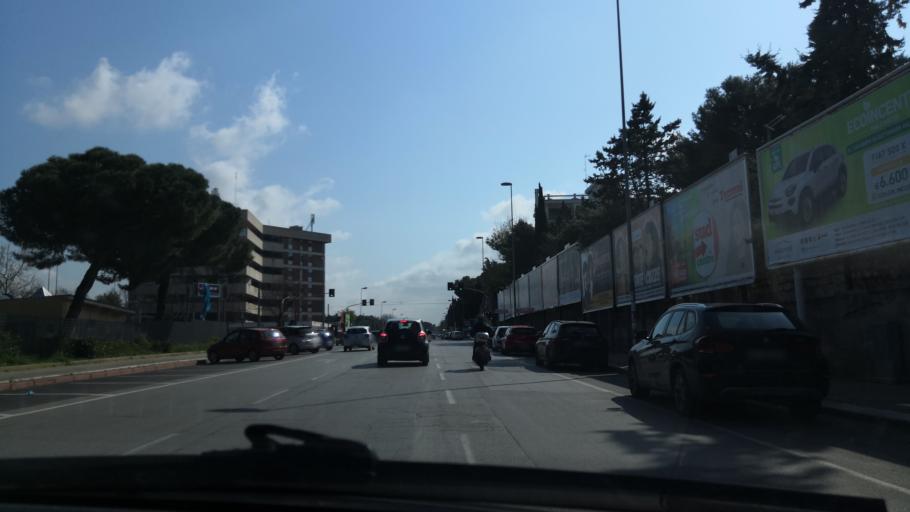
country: IT
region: Apulia
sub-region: Provincia di Bari
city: Bari
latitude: 41.1015
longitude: 16.8736
